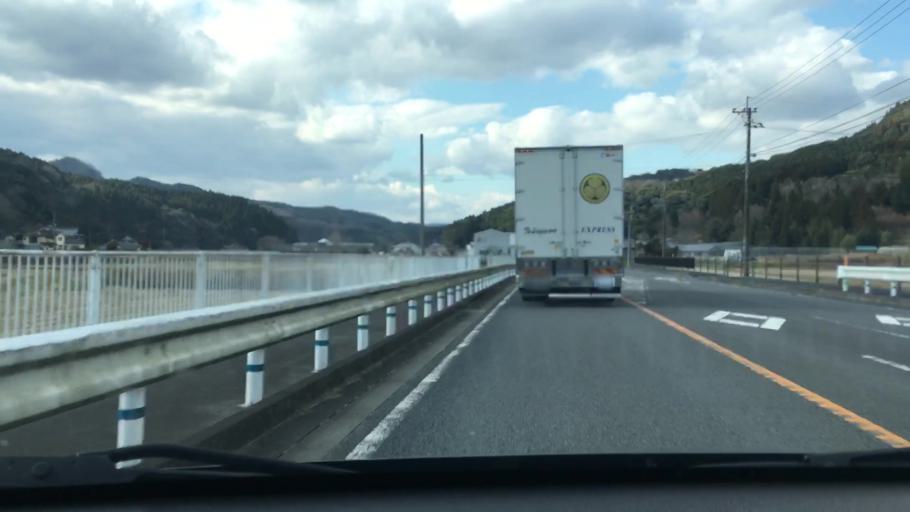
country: JP
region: Oita
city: Usuki
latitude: 33.0052
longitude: 131.7256
